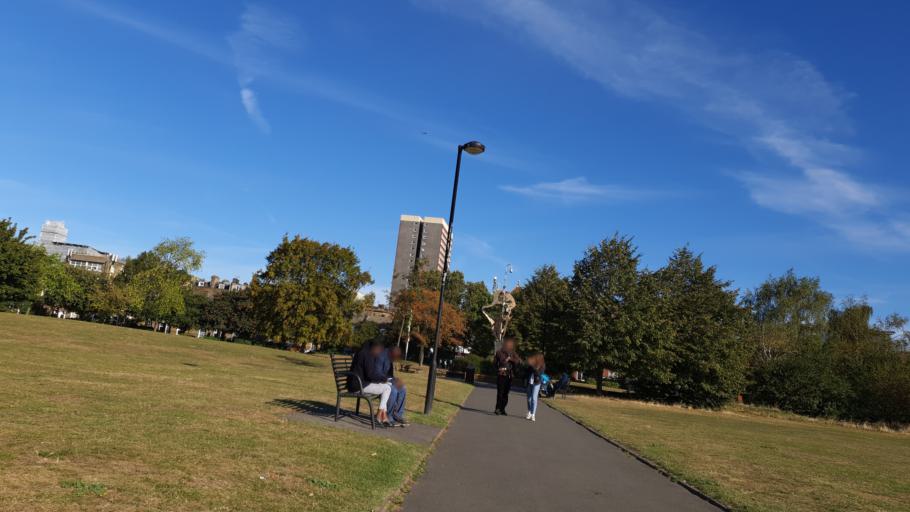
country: GB
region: England
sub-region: Greater London
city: Bethnal Green
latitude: 51.5253
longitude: -0.0612
